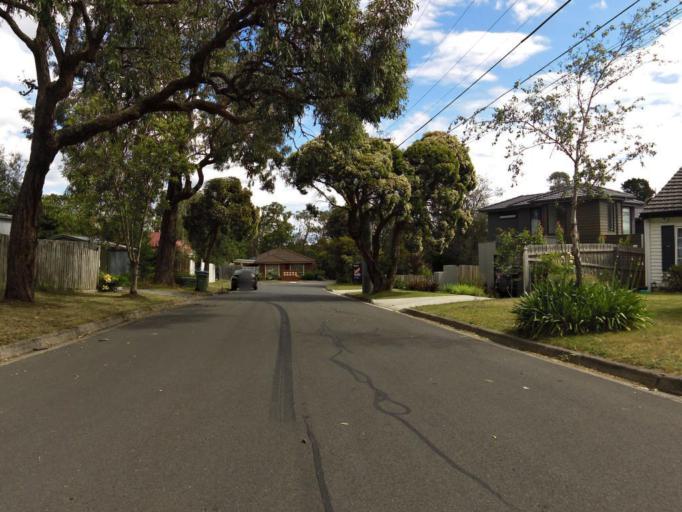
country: AU
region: Victoria
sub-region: Maroondah
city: Ringwood East
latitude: -37.8197
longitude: 145.2409
